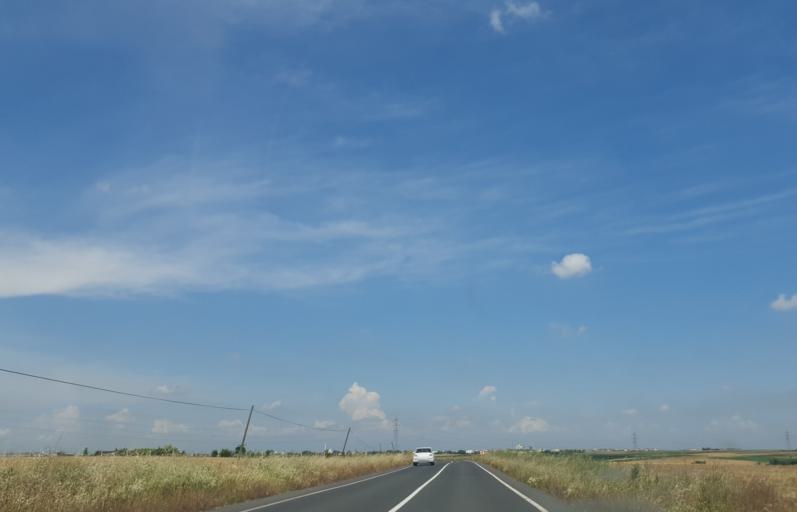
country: TR
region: Kirklareli
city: Buyukkaristiran
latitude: 41.2501
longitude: 27.6172
